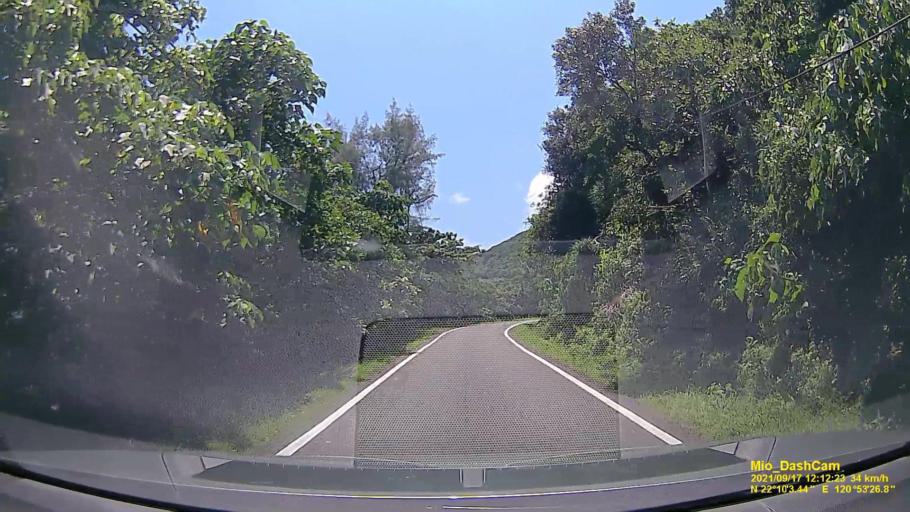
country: TW
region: Taiwan
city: Hengchun
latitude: 22.1676
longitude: 120.8908
